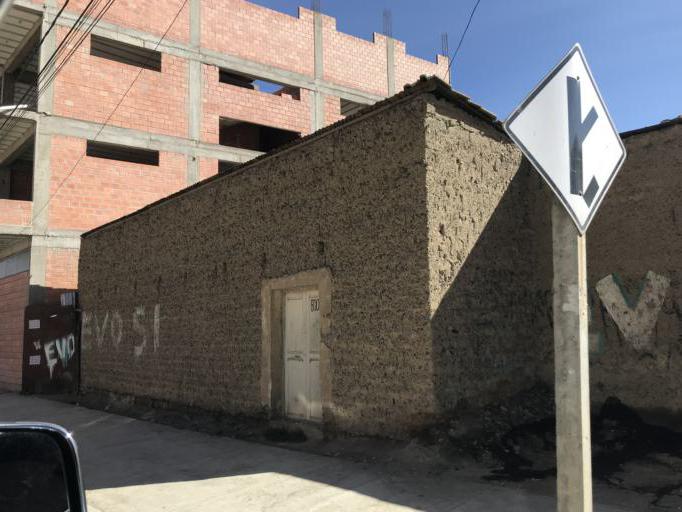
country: BO
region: La Paz
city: La Paz
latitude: -16.4867
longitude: -68.1762
